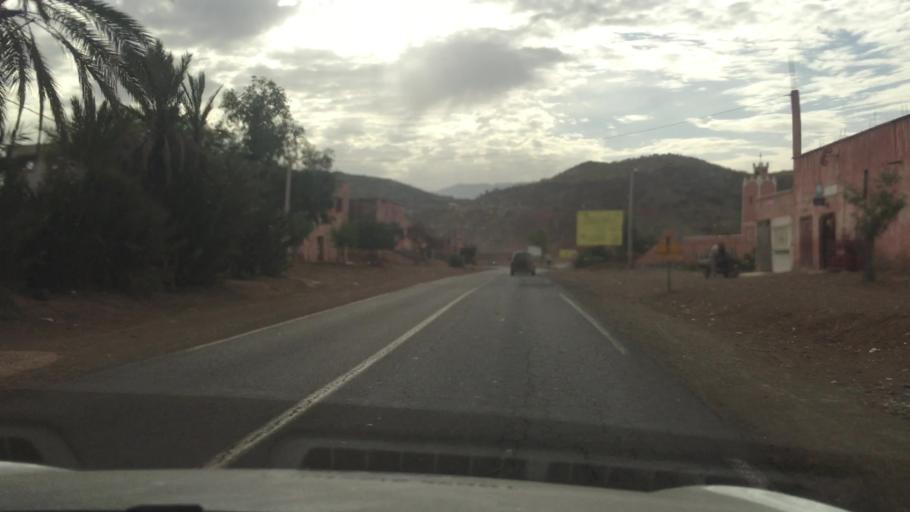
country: MA
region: Marrakech-Tensift-Al Haouz
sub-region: Al-Haouz
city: Touama
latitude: 31.5468
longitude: -7.5736
